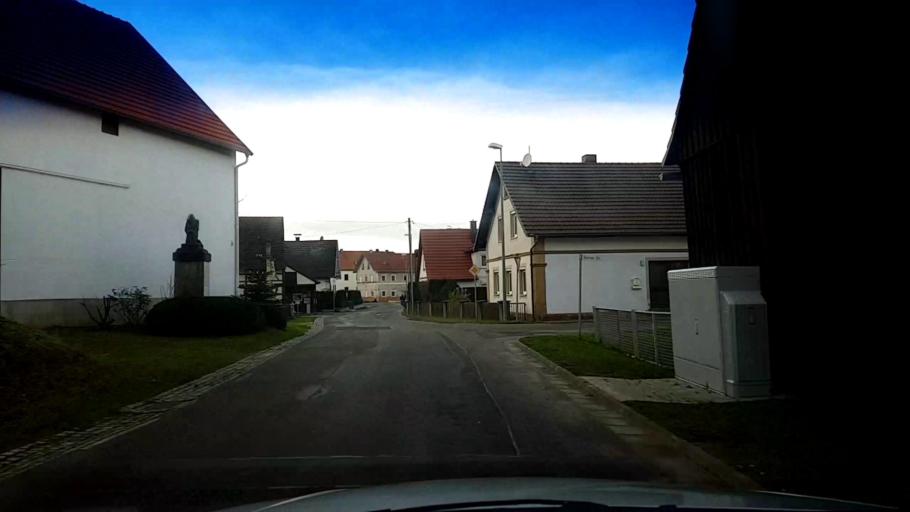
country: DE
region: Bavaria
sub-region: Upper Franconia
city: Litzendorf
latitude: 49.9406
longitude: 10.9979
